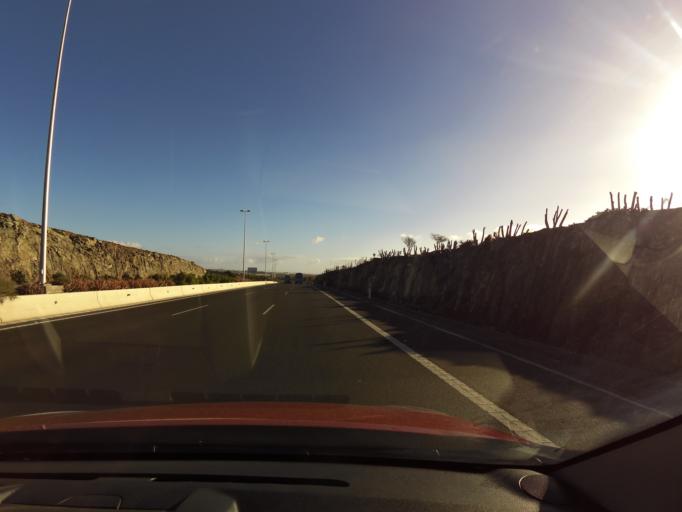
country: ES
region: Canary Islands
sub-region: Provincia de Las Palmas
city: Playa del Ingles
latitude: 27.7894
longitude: -15.5008
